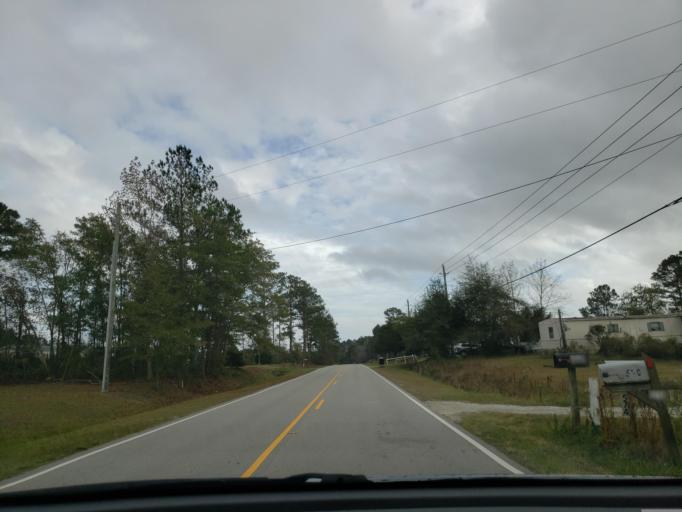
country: US
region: North Carolina
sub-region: Onslow County
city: Jacksonville
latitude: 34.7050
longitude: -77.5738
